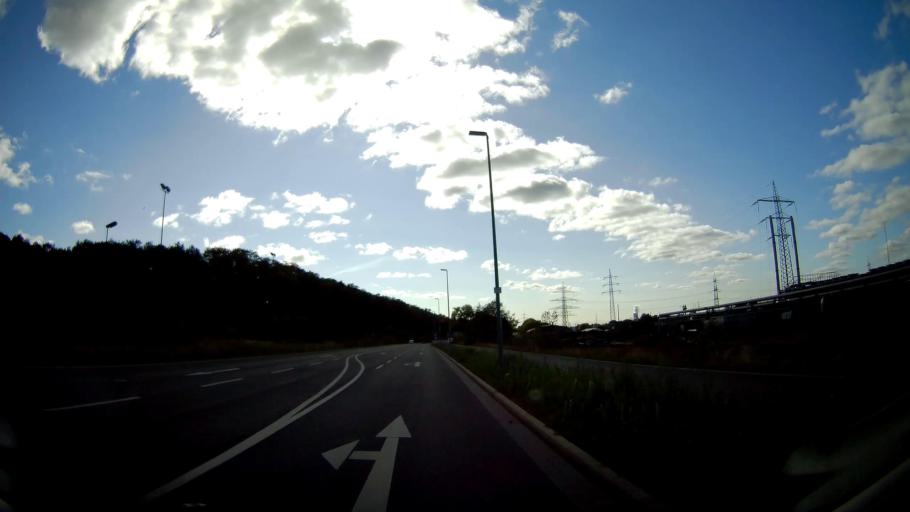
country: DE
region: North Rhine-Westphalia
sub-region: Regierungsbezirk Dusseldorf
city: Dinslaken
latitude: 51.5806
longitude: 6.7643
